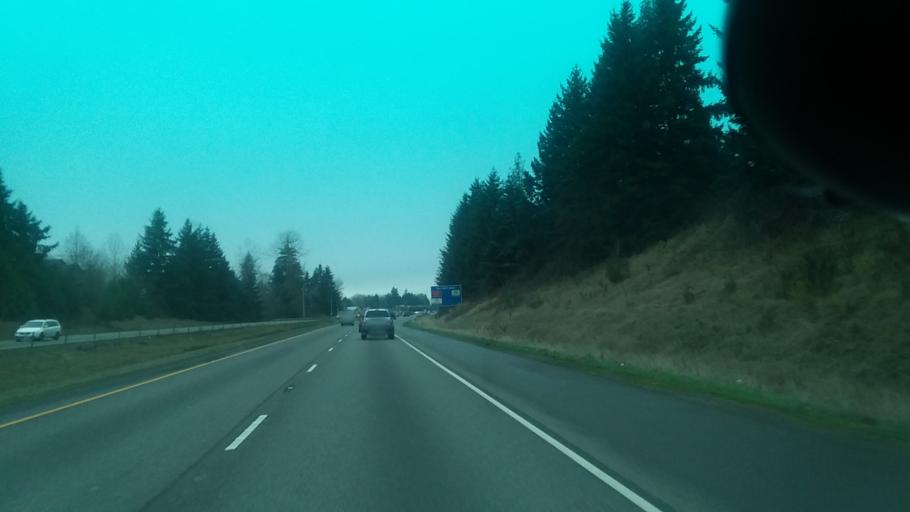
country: US
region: Washington
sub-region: Pierce County
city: Summit
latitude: 47.1578
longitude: -122.3454
